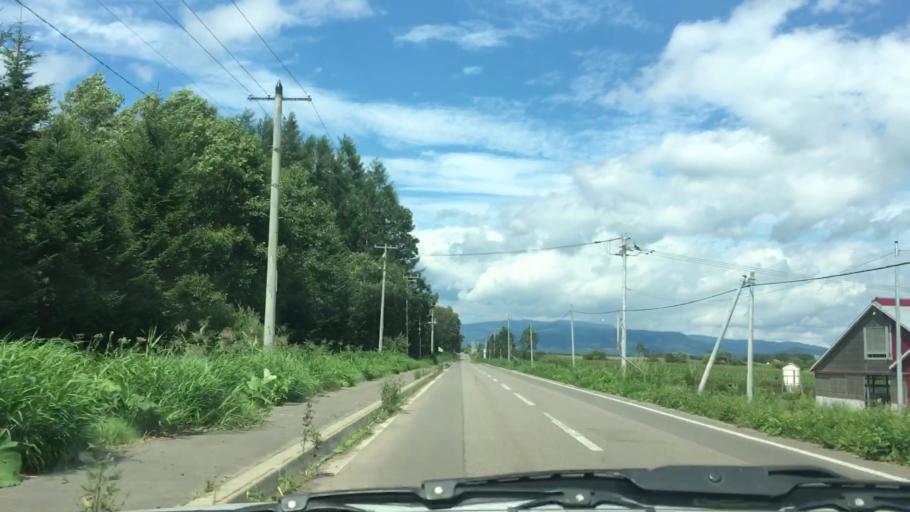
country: JP
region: Hokkaido
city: Otofuke
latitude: 43.2689
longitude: 143.3864
